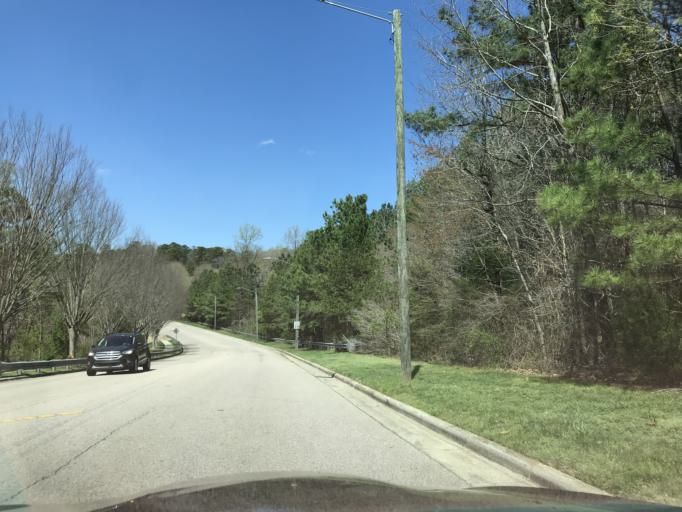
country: US
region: North Carolina
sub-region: Wake County
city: Cary
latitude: 35.8740
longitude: -78.7193
